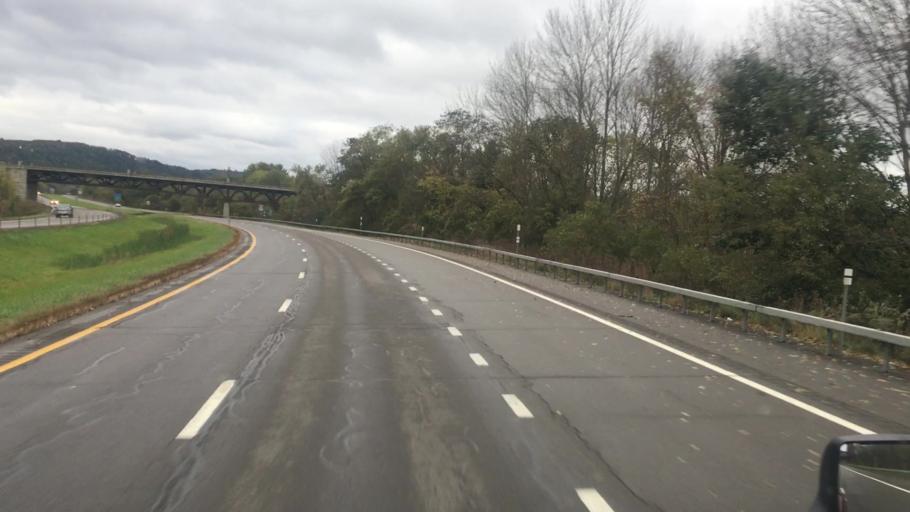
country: US
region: New York
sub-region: Tioga County
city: Owego
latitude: 42.1010
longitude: -76.2569
